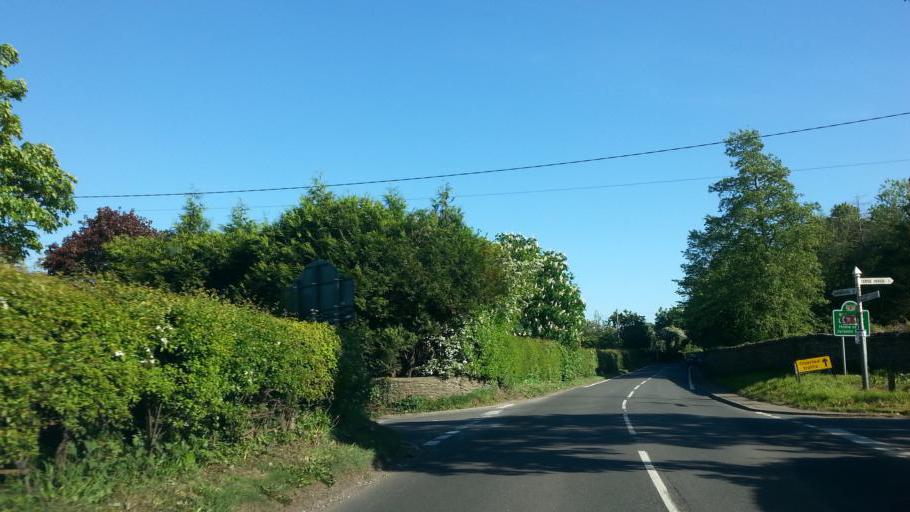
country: GB
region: England
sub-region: Dorset
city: Stalbridge
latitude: 50.9708
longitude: -2.3882
